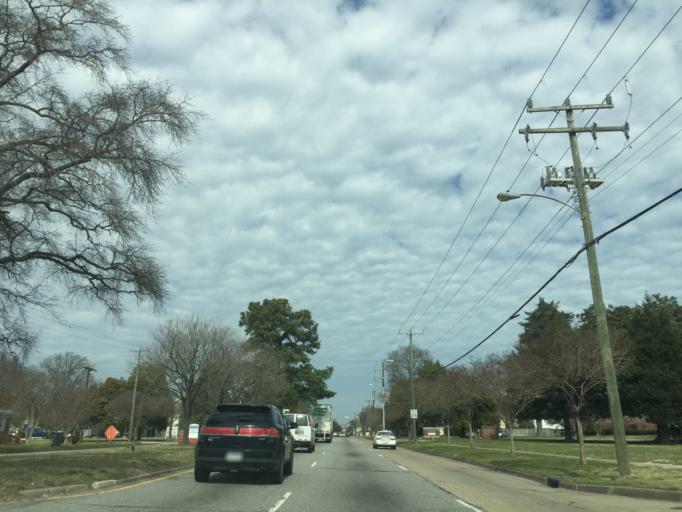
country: US
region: Virginia
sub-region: City of Norfolk
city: Norfolk
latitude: 36.9032
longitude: -76.2775
